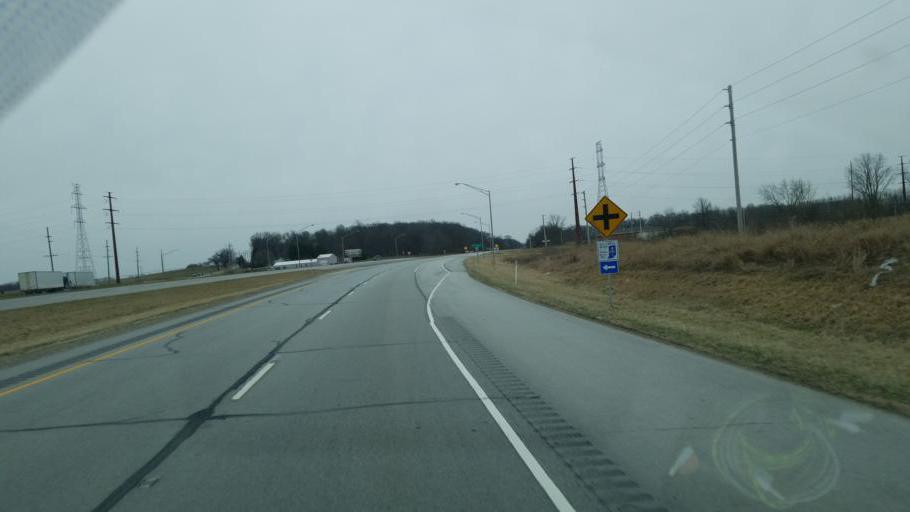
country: US
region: Indiana
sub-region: Marshall County
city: Plymouth
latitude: 41.2900
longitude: -86.2712
